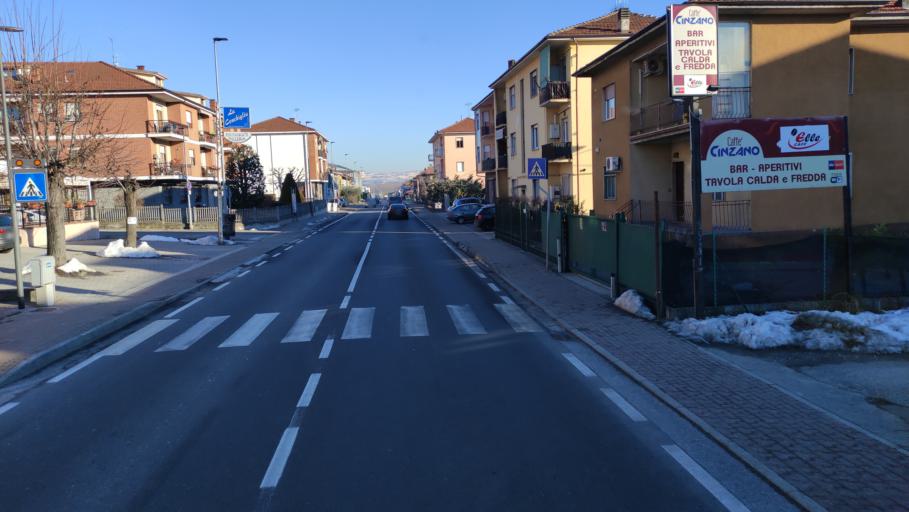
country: IT
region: Piedmont
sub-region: Provincia di Cuneo
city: Cinzano
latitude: 44.6937
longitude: 7.9178
